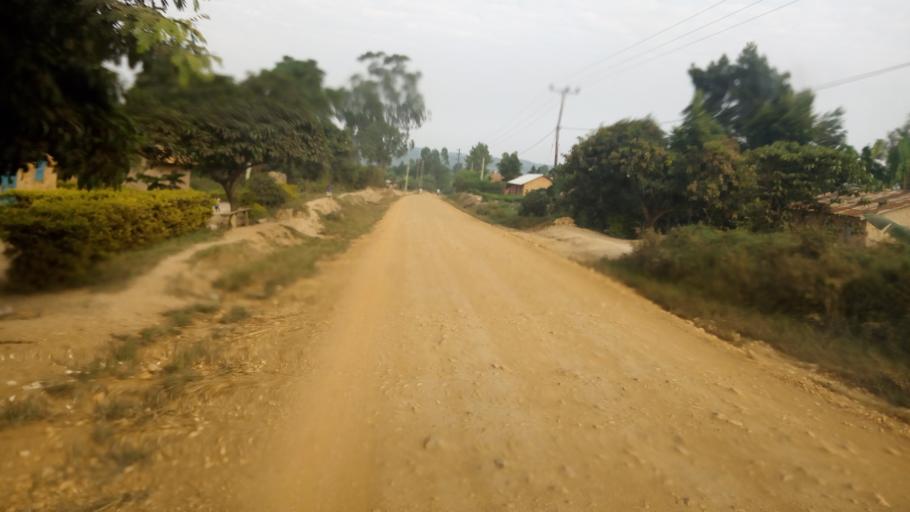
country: UG
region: Western Region
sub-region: Kanungu District
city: Ntungamo
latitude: -0.8393
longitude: 29.6501
